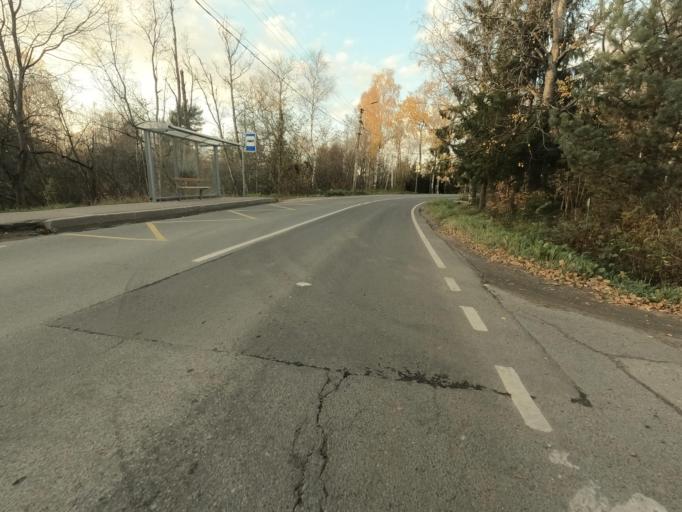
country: RU
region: St.-Petersburg
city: Beloostrov
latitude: 60.1599
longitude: 30.0058
